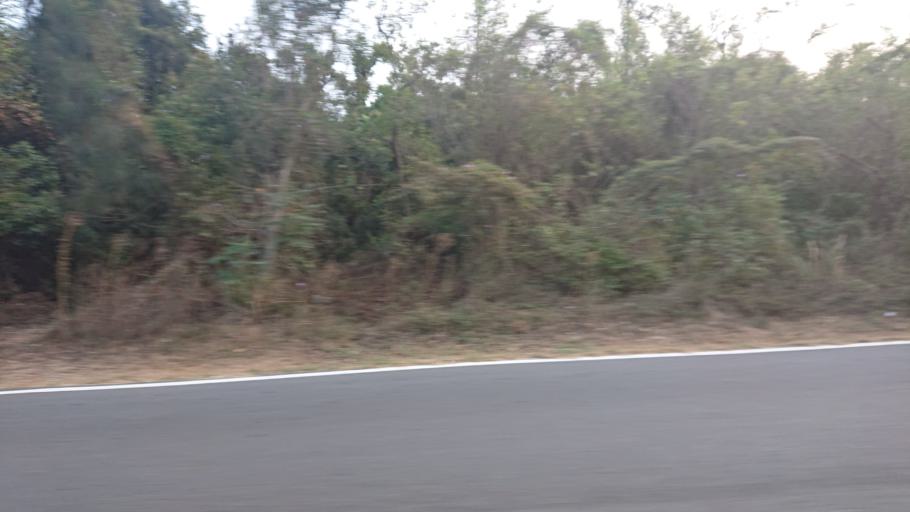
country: CN
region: Fujian
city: Dadeng
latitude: 24.4816
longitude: 118.4333
